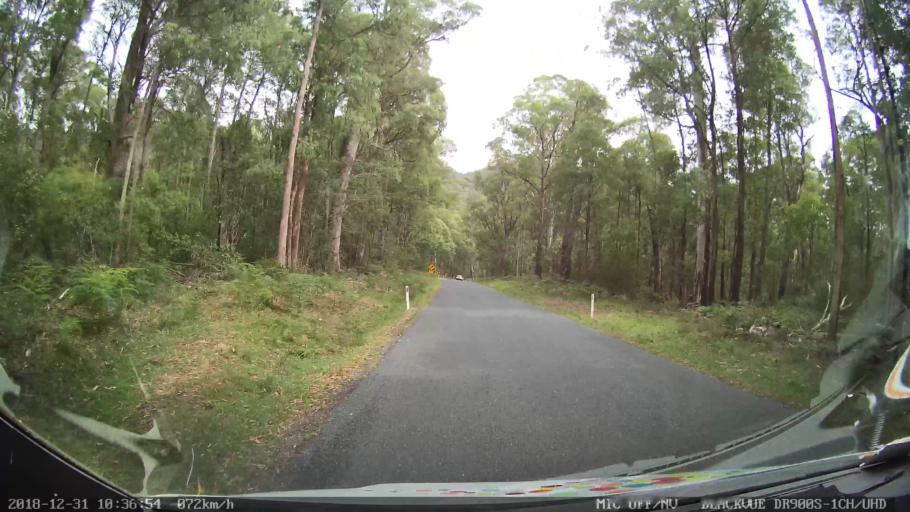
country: AU
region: New South Wales
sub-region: Snowy River
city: Jindabyne
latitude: -36.4210
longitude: 148.1702
